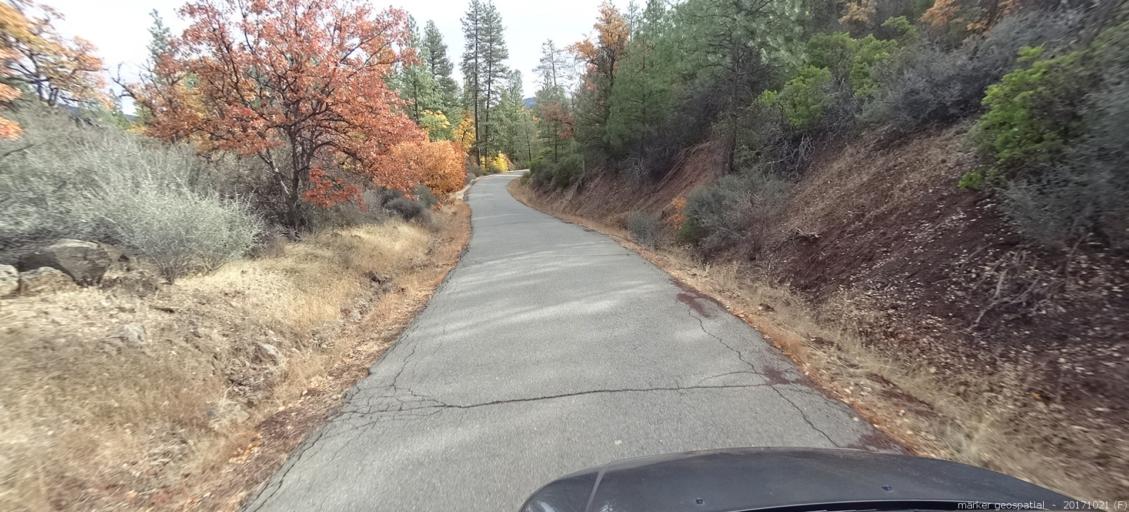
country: US
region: California
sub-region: Shasta County
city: Burney
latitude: 40.9653
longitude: -121.5645
